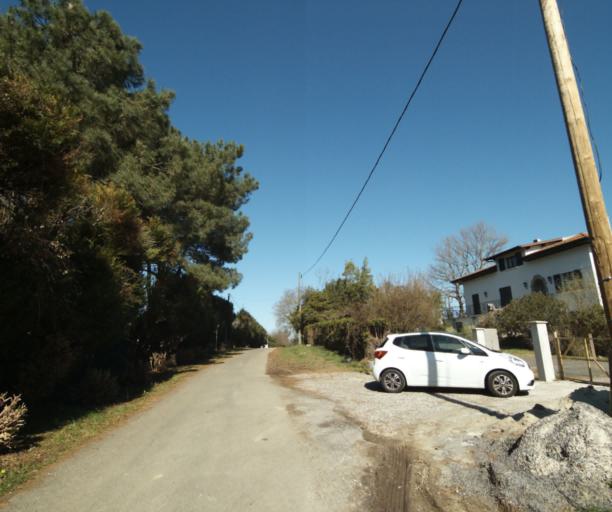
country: FR
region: Aquitaine
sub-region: Departement des Pyrenees-Atlantiques
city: Ciboure
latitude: 43.3620
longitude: -1.6695
